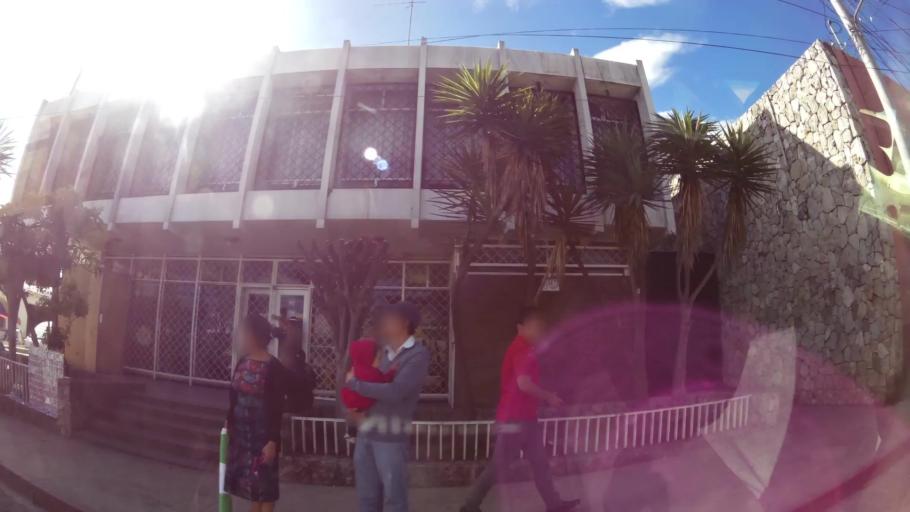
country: GT
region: Solola
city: Solola
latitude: 14.7717
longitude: -91.1827
